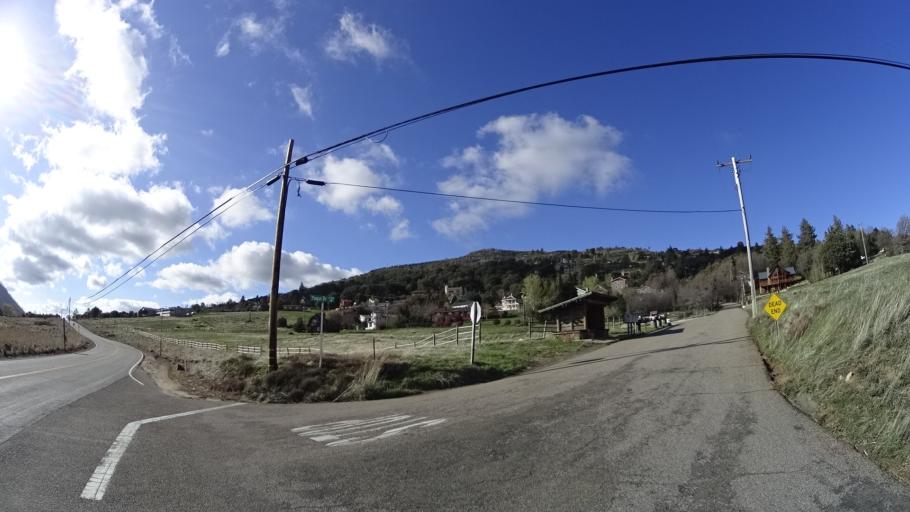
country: US
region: California
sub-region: San Diego County
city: Julian
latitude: 32.9910
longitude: -116.5801
